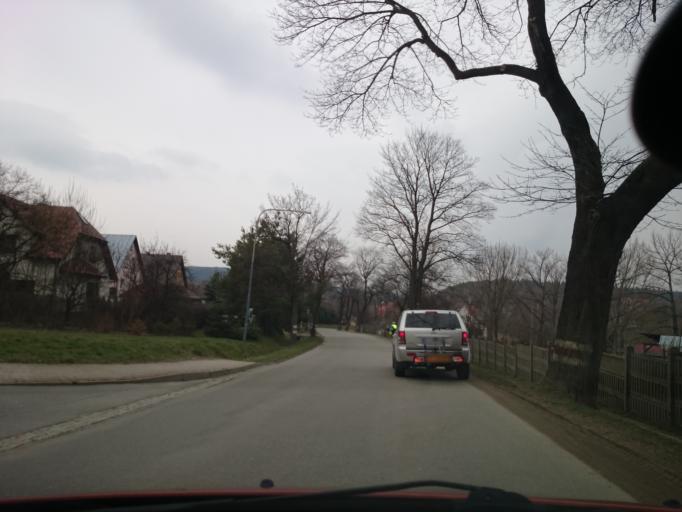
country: PL
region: Lower Silesian Voivodeship
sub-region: Powiat klodzki
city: Polanica-Zdroj
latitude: 50.3950
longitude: 16.5212
